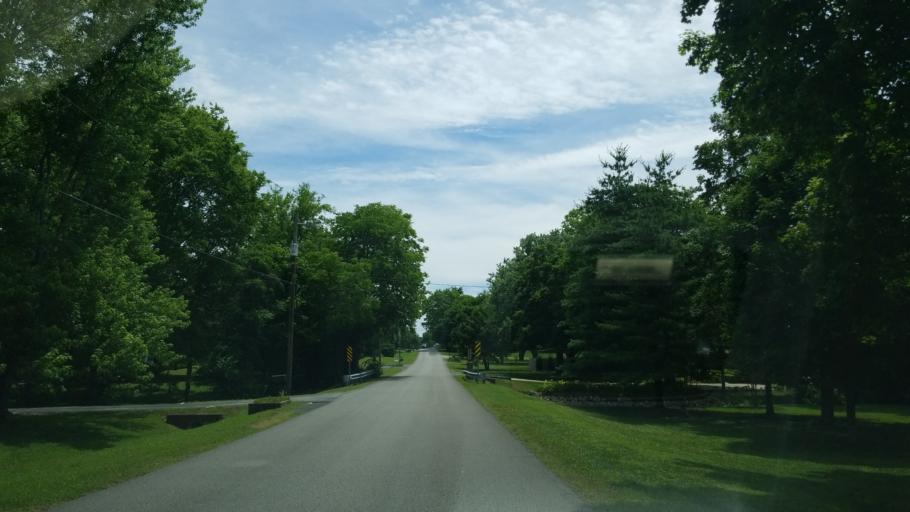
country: US
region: Tennessee
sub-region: Williamson County
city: Brentwood
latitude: 36.0298
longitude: -86.8028
